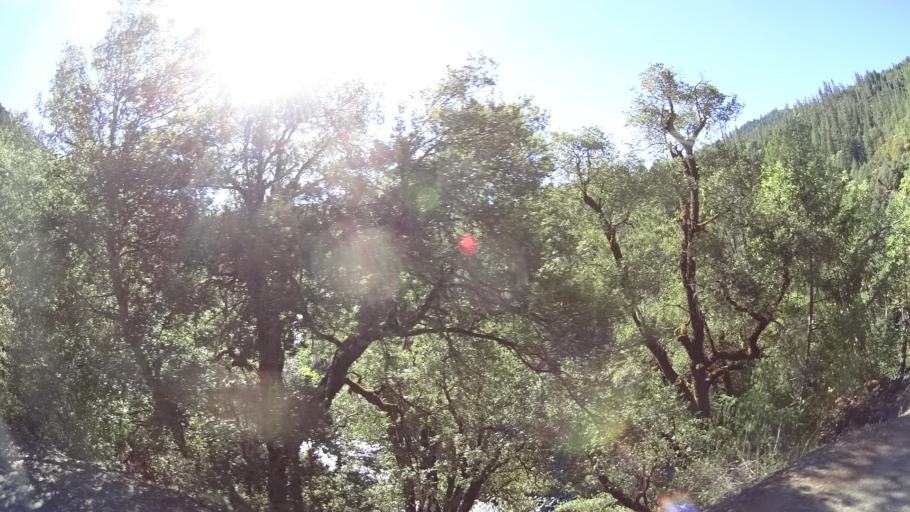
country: US
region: California
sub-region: Humboldt County
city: Willow Creek
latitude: 41.1983
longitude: -123.2175
